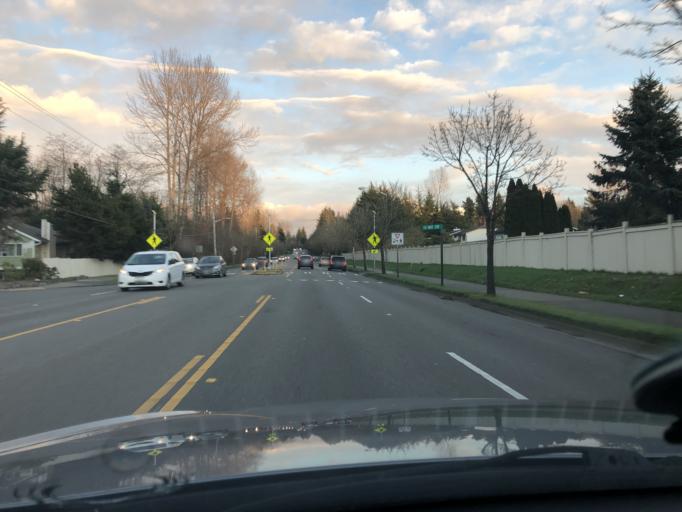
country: US
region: Washington
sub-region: King County
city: Federal Way
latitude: 47.3151
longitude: -122.3548
